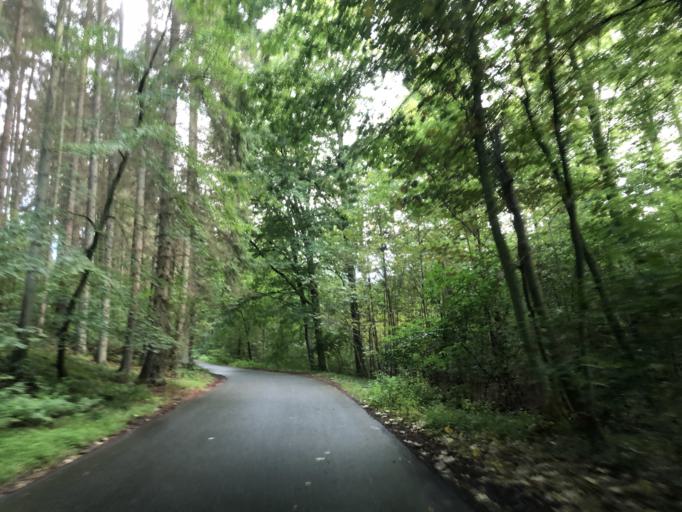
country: DK
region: South Denmark
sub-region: Vejle Kommune
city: Borkop
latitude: 55.6843
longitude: 9.6008
